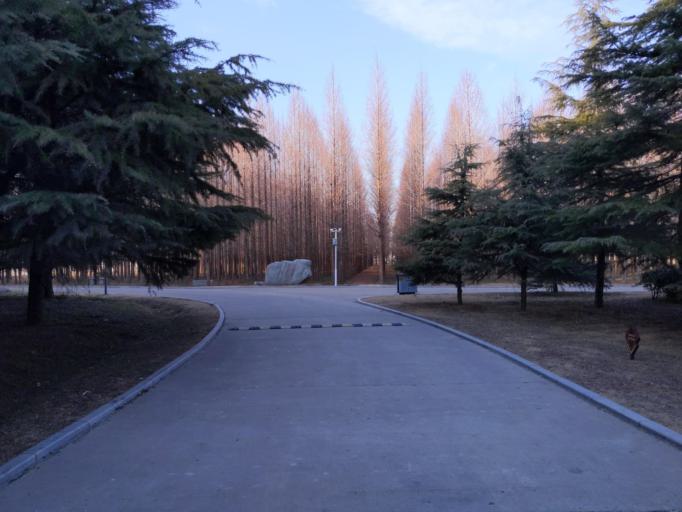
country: CN
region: Henan Sheng
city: Puyang
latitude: 35.7798
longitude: 114.9515
